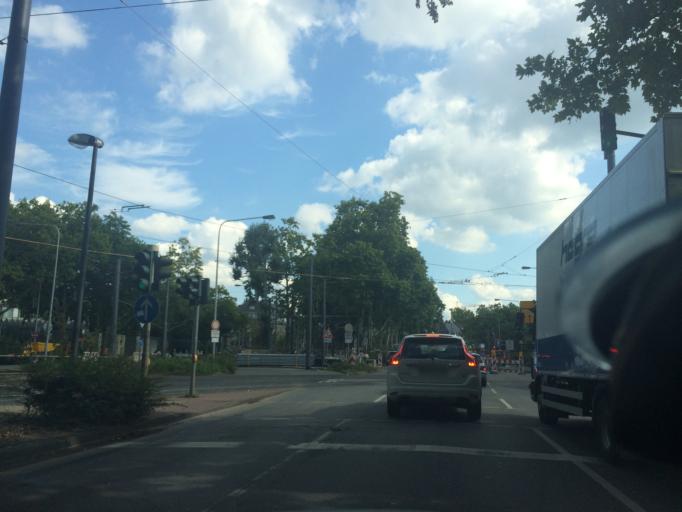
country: DE
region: Hesse
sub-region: Regierungsbezirk Darmstadt
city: Frankfurt am Main
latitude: 50.0987
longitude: 8.6692
